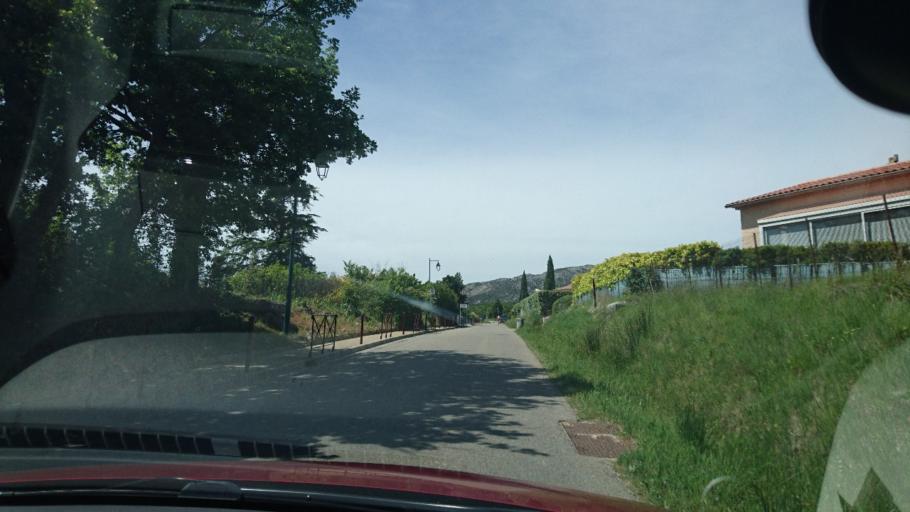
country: FR
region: Provence-Alpes-Cote d'Azur
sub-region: Departement du Vaucluse
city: Bedoin
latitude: 44.1272
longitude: 5.1785
